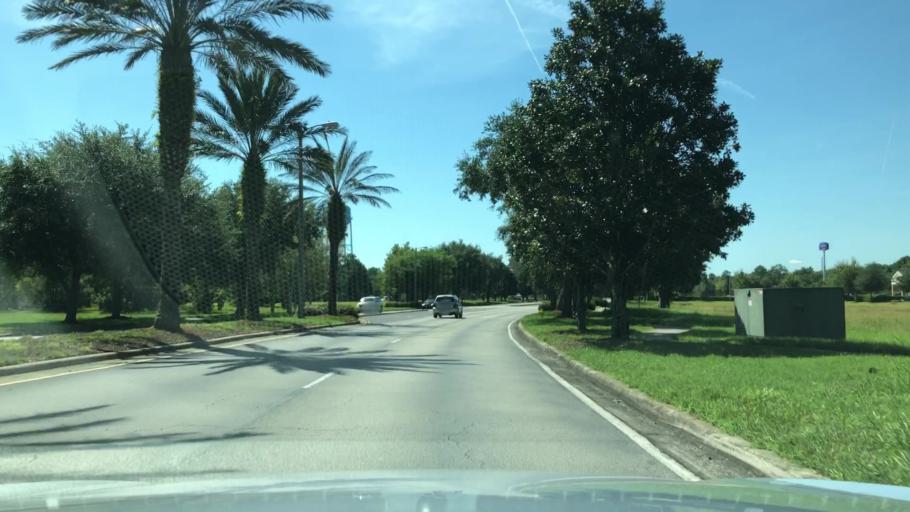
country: US
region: Florida
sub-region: Saint Johns County
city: Saint Augustine
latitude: 29.9218
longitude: -81.4104
